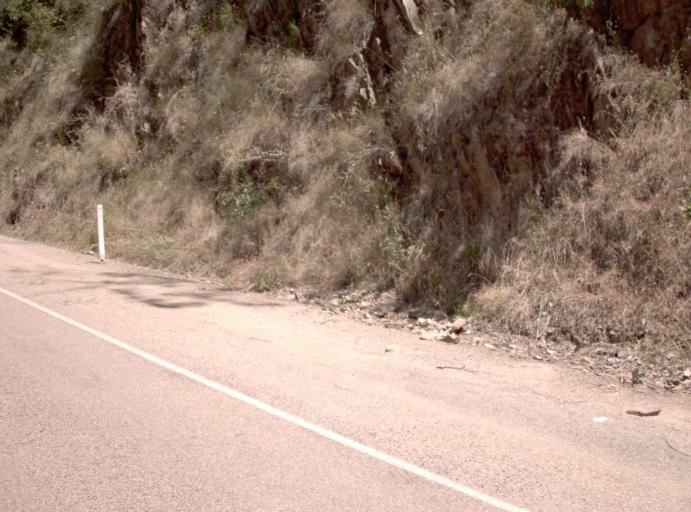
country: AU
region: Victoria
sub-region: East Gippsland
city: Bairnsdale
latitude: -37.4679
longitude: 147.8284
